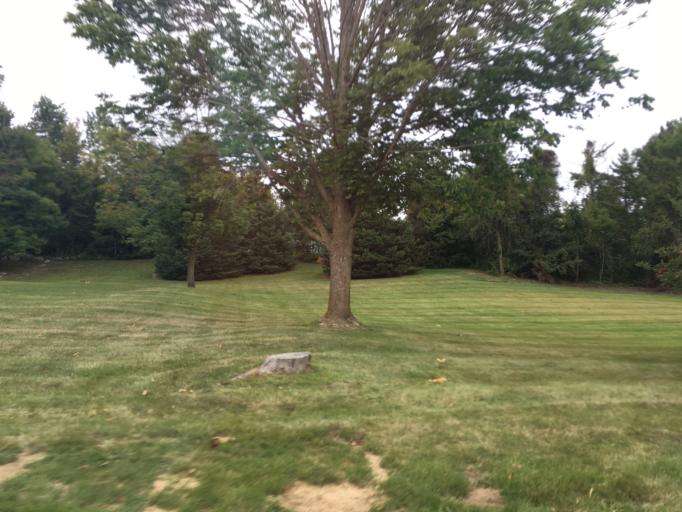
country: US
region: Michigan
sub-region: Lapeer County
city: Barnes Lake-Millers Lake
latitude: 43.3340
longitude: -83.3426
